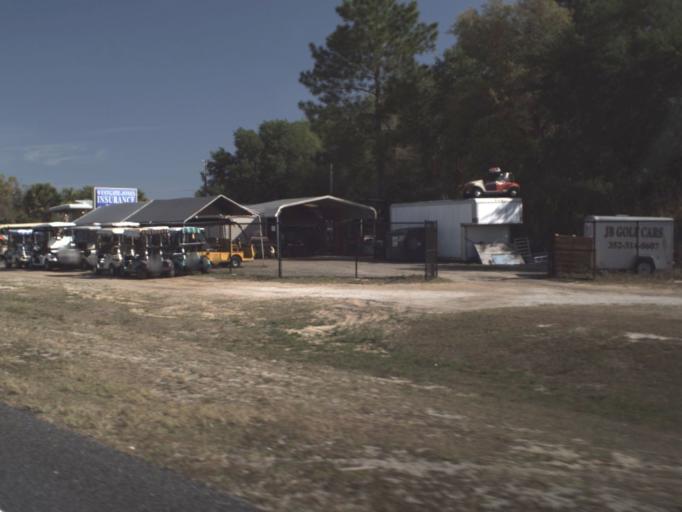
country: US
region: Florida
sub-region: Lake County
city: Hawthorne
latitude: 28.7277
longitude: -81.8636
